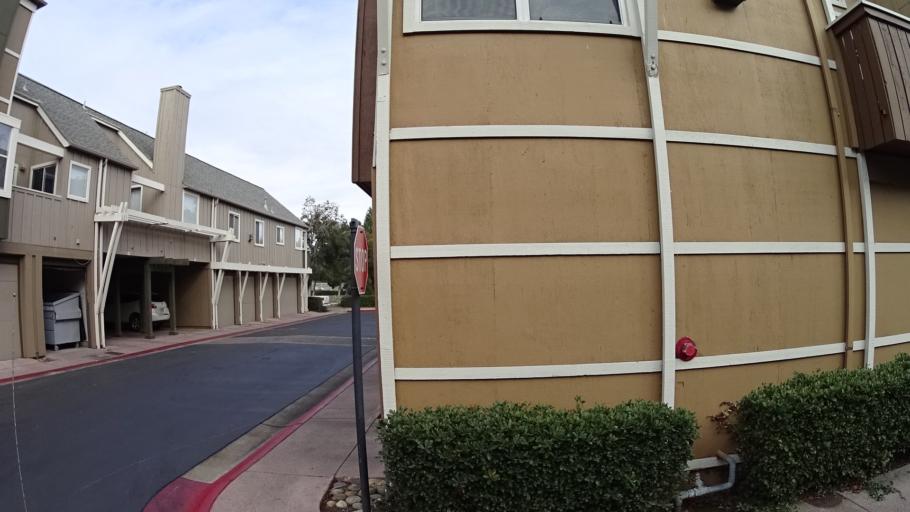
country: US
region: California
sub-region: San Mateo County
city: Redwood Shores
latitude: 37.5357
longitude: -122.2395
